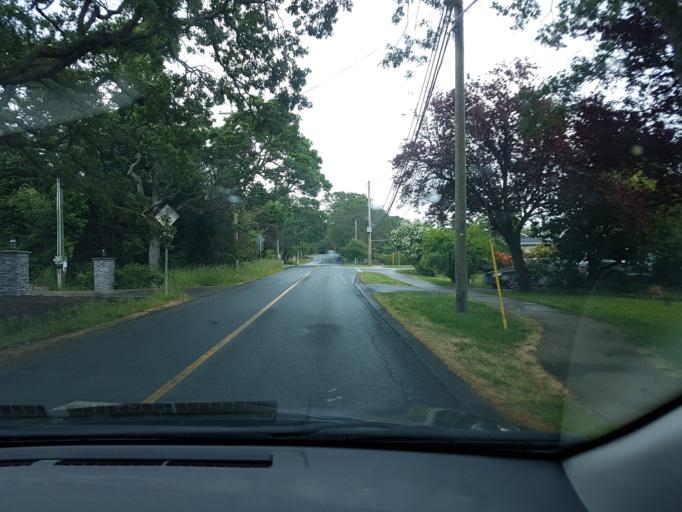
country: CA
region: British Columbia
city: Oak Bay
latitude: 48.4777
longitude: -123.3447
